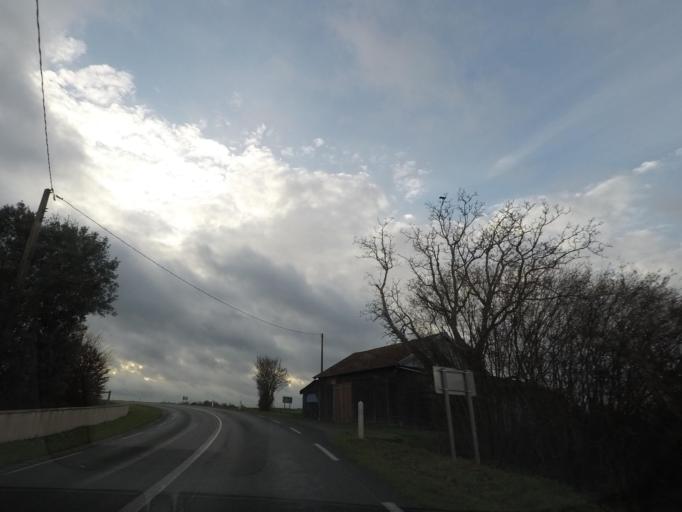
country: FR
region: Pays de la Loire
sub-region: Departement de la Sarthe
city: Vibraye
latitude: 48.1124
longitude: 0.7078
